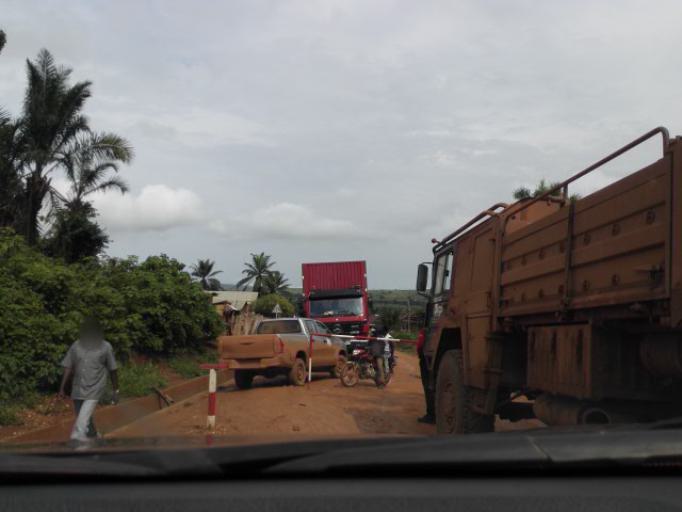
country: CD
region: Eastern Province
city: Bunia
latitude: 1.3659
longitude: 29.7646
